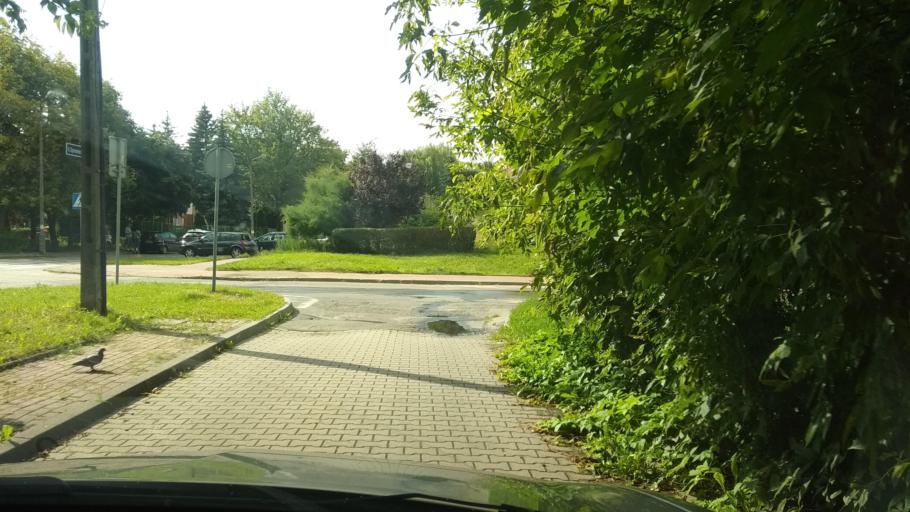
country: PL
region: Masovian Voivodeship
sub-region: Powiat pruszkowski
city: Pruszkow
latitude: 52.1621
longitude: 20.8207
